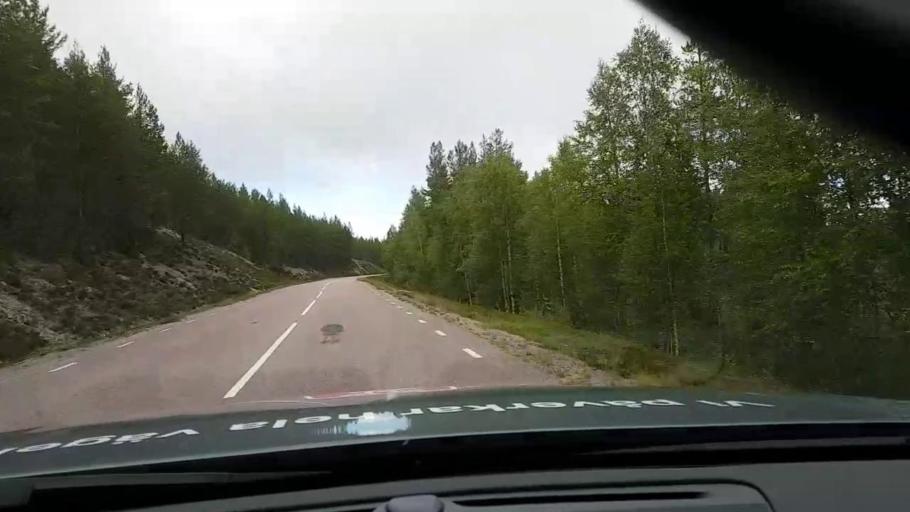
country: SE
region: Vaesterbotten
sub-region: Asele Kommun
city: Asele
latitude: 63.8788
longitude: 17.3559
